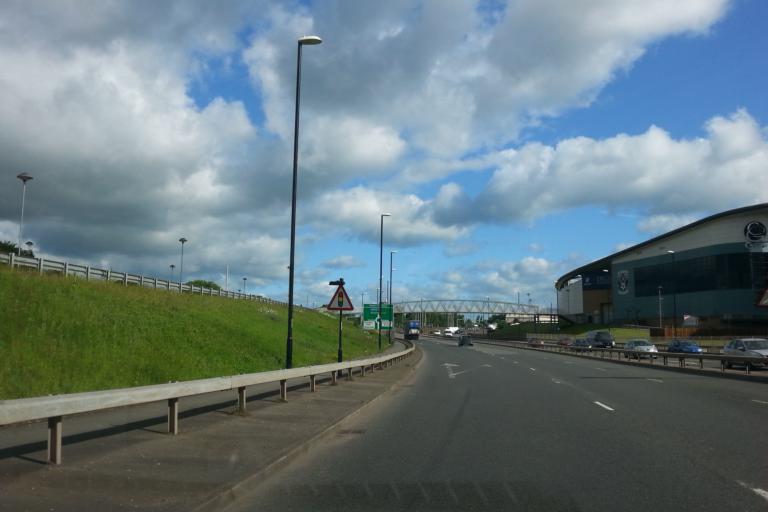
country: GB
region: England
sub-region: Warwickshire
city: Exhall
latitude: 52.4466
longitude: -1.4975
